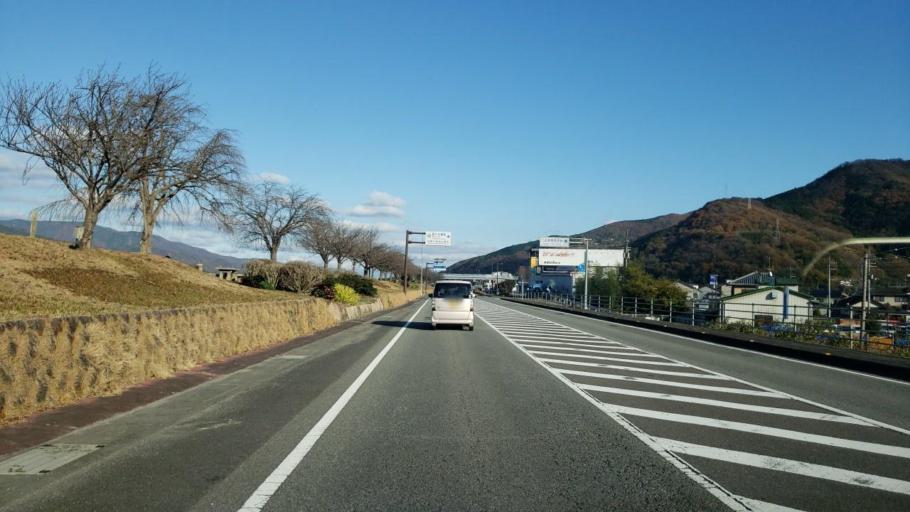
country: JP
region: Tokushima
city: Wakimachi
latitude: 34.0425
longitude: 134.0572
